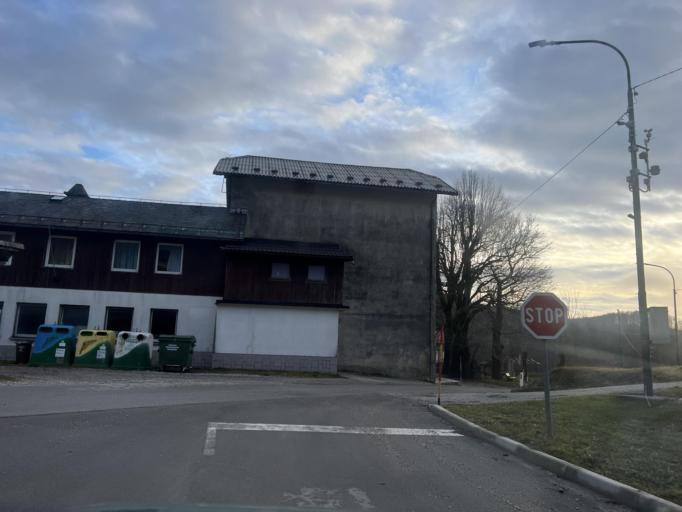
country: SI
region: Nova Gorica
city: Sempas
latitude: 46.0120
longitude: 13.7919
